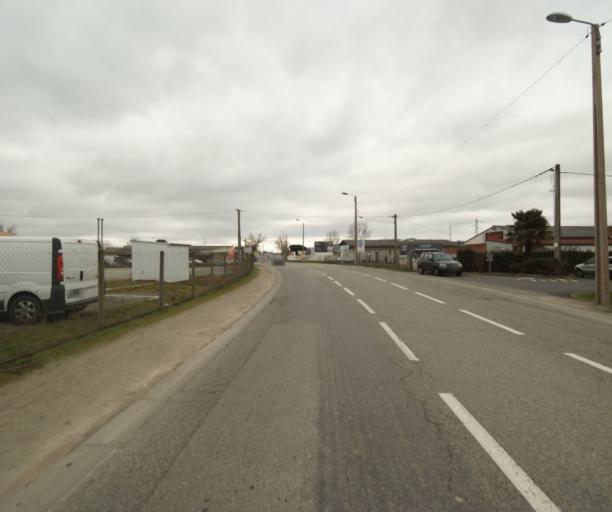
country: FR
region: Midi-Pyrenees
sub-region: Departement de l'Ariege
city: Pamiers
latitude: 43.1260
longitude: 1.6210
